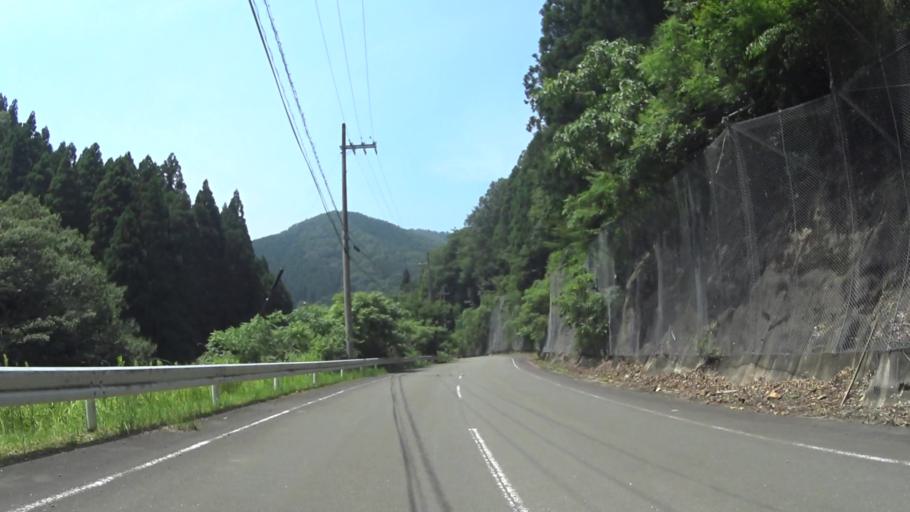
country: JP
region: Kyoto
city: Maizuru
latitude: 35.3176
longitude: 135.4433
